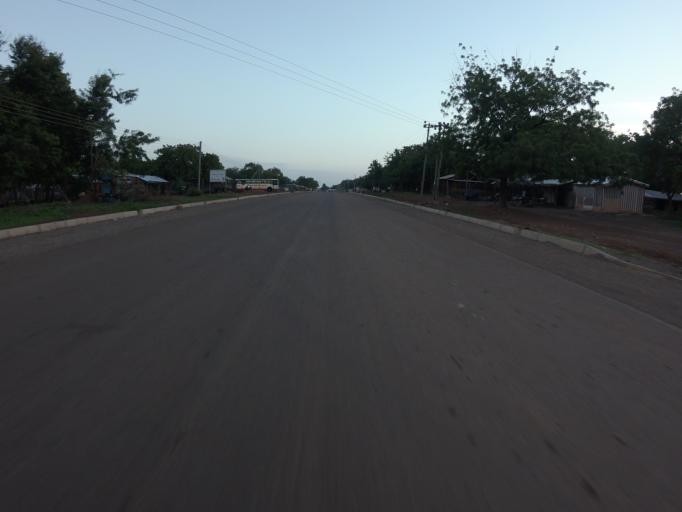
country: GH
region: Northern
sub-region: Yendi
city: Yendi
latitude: 9.9256
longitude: -0.2122
